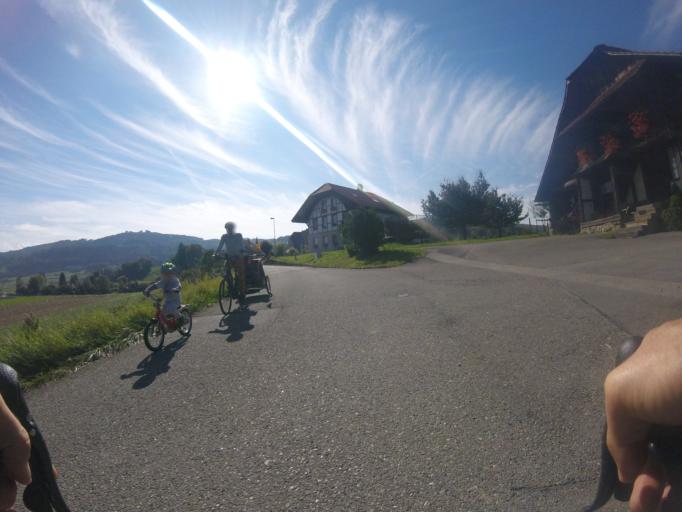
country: CH
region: Bern
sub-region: Bern-Mittelland District
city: Muri
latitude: 46.9206
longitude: 7.4808
